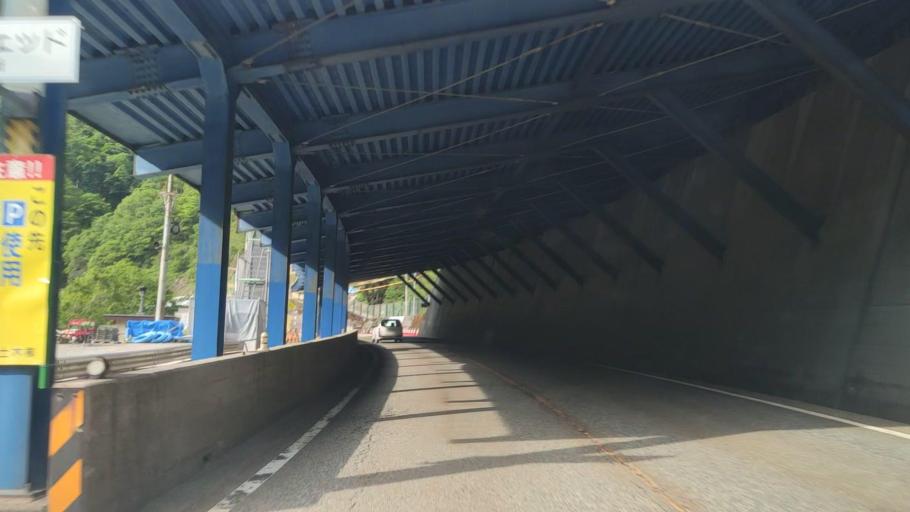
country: JP
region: Toyama
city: Yatsuomachi-higashikumisaka
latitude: 36.3797
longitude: 137.2797
